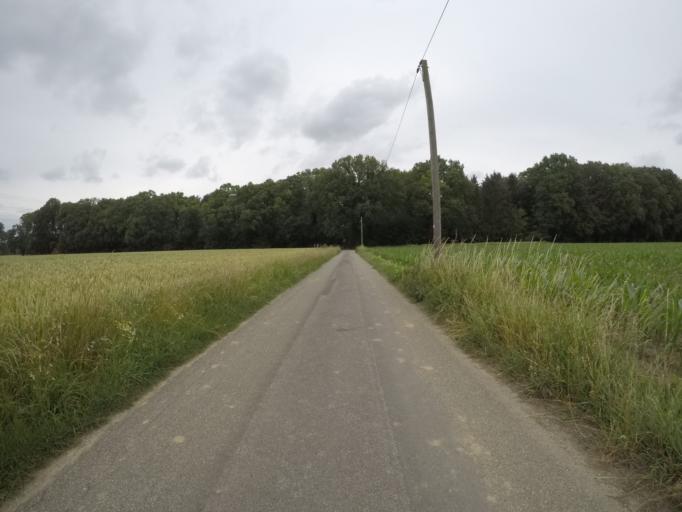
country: DE
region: North Rhine-Westphalia
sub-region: Regierungsbezirk Munster
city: Isselburg
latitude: 51.8447
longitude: 6.4467
